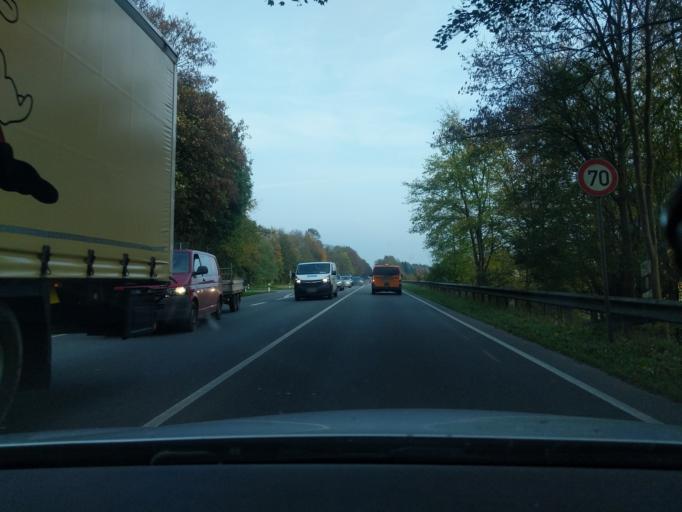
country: DE
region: Lower Saxony
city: Stade
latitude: 53.5836
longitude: 9.4729
